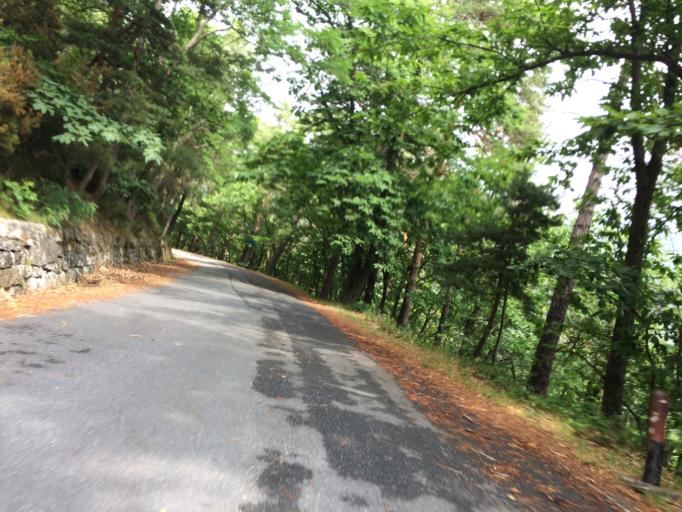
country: IT
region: Liguria
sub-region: Provincia di Imperia
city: Bajardo
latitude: 43.8955
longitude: 7.7318
